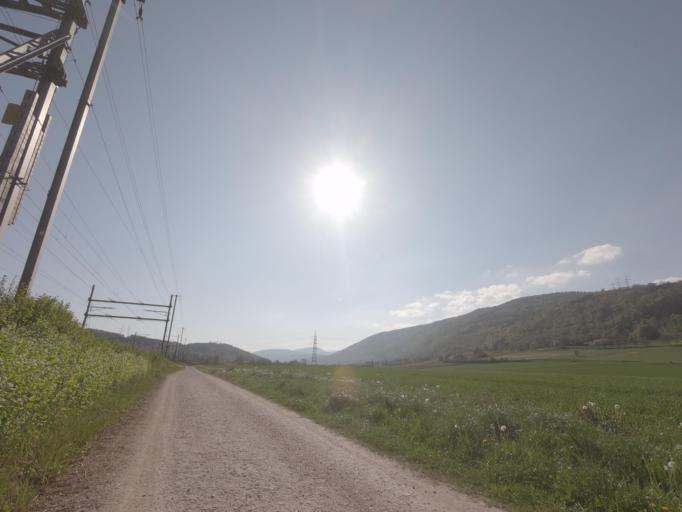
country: CH
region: Bern
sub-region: Biel/Bienne District
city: Lengnau
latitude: 47.1764
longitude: 7.3597
